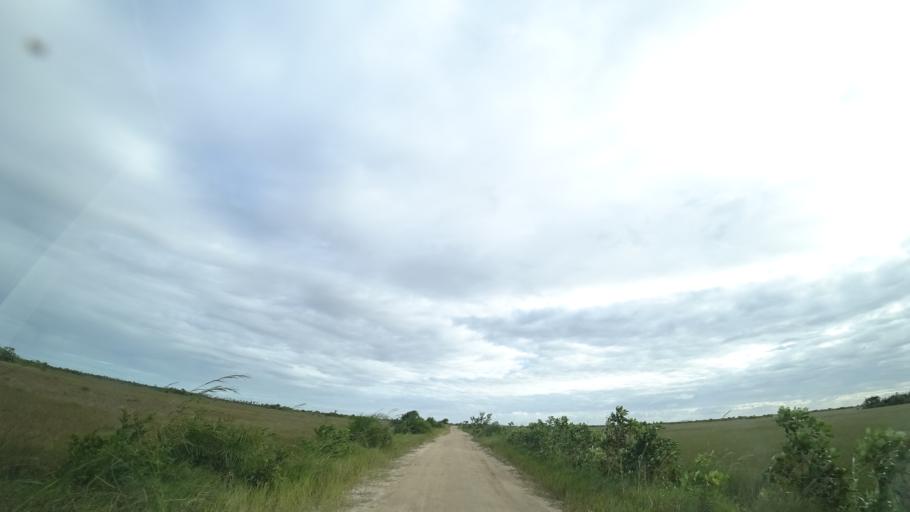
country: MZ
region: Sofala
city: Beira
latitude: -19.6970
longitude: 35.0320
